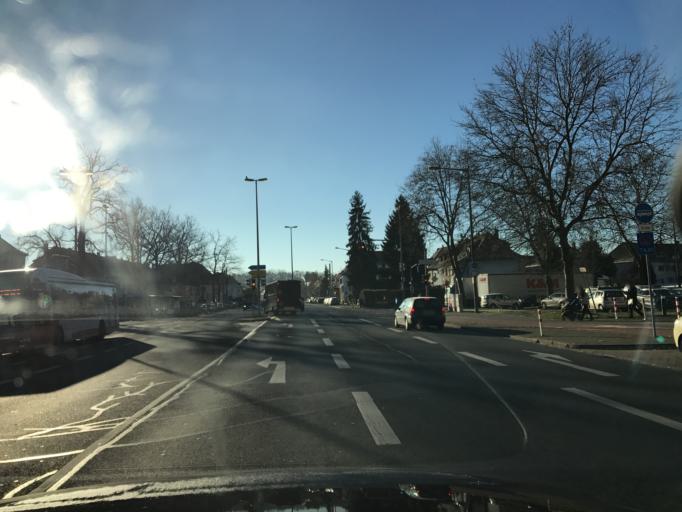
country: DE
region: Bavaria
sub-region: Regierungsbezirk Mittelfranken
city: Nuernberg
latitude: 49.4848
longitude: 11.1050
